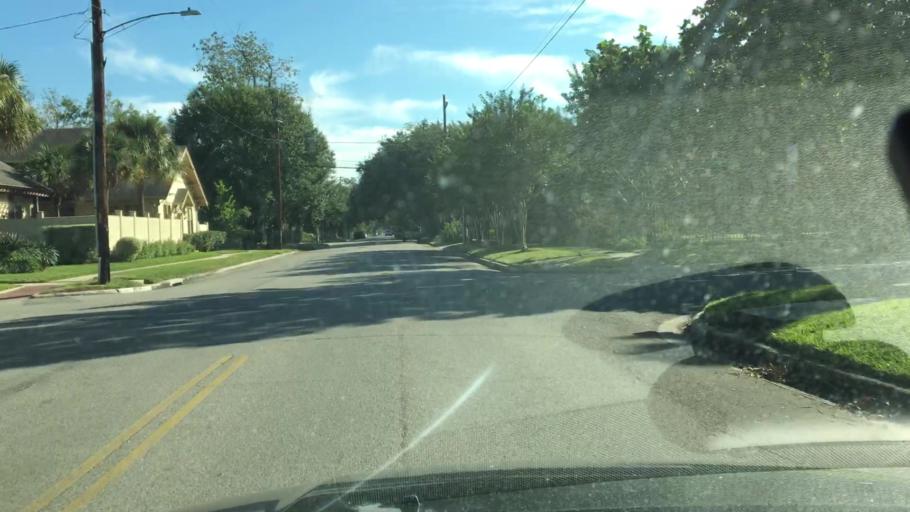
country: US
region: Texas
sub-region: Harris County
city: Houston
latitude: 29.7962
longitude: -95.3967
